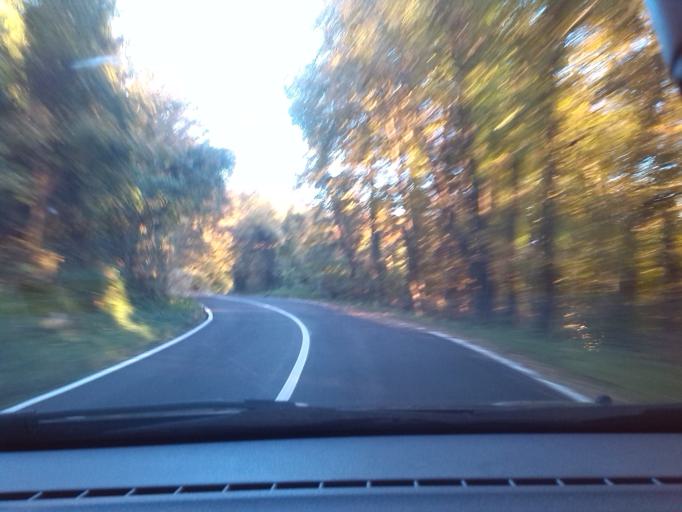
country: IT
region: Friuli Venezia Giulia
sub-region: Provincia di Udine
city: Savogna
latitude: 46.1954
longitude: 13.5304
